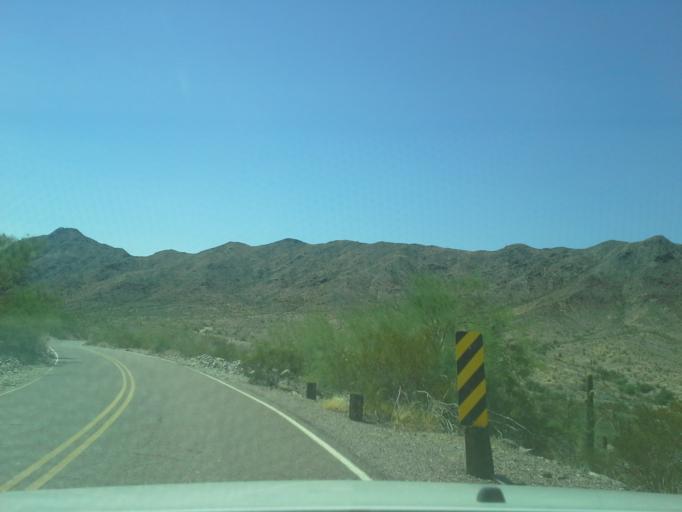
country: US
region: Arizona
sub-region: Maricopa County
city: Laveen
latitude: 33.3323
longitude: -112.0927
